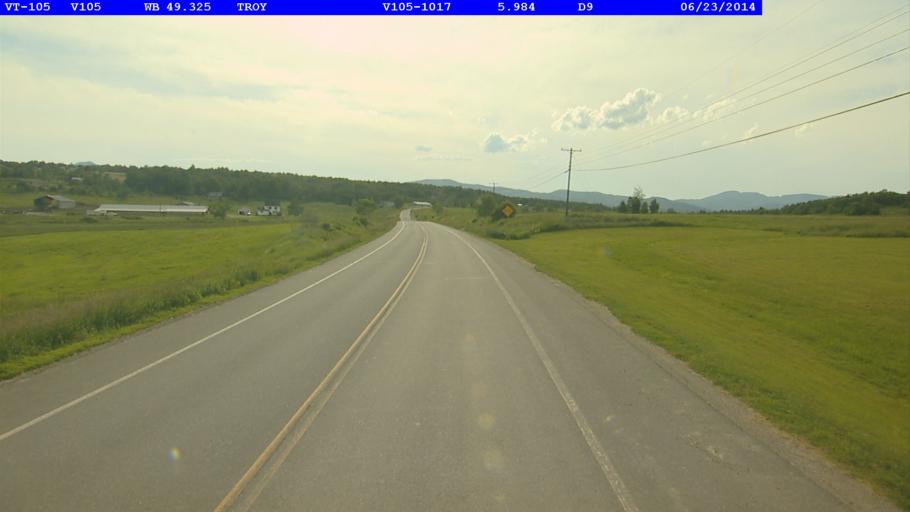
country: US
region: Vermont
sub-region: Orleans County
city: Newport
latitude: 44.9797
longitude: -72.3425
